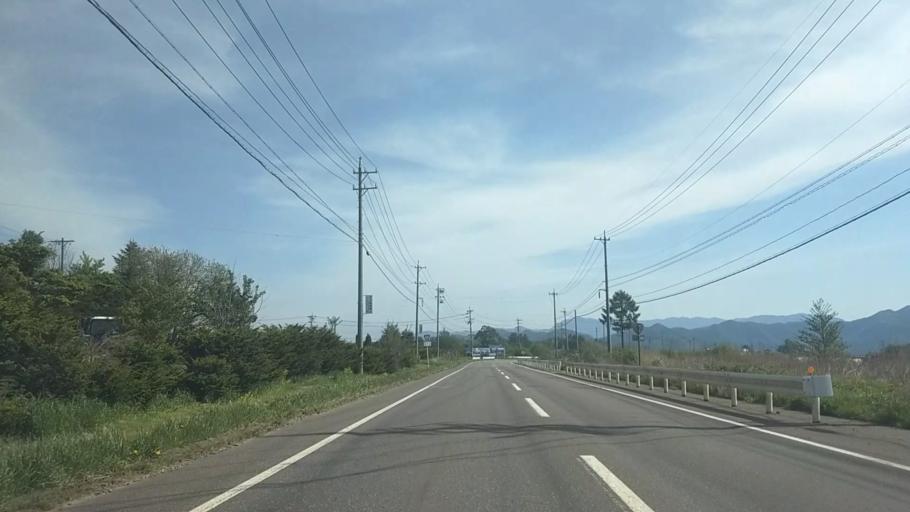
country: JP
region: Nagano
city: Saku
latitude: 35.9848
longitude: 138.4853
